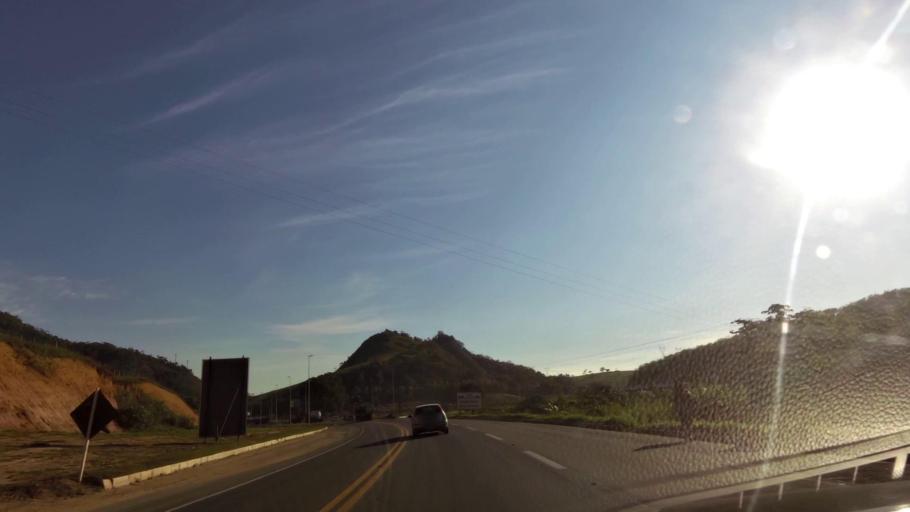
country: BR
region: Espirito Santo
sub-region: Guarapari
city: Guarapari
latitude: -20.5232
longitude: -40.4789
